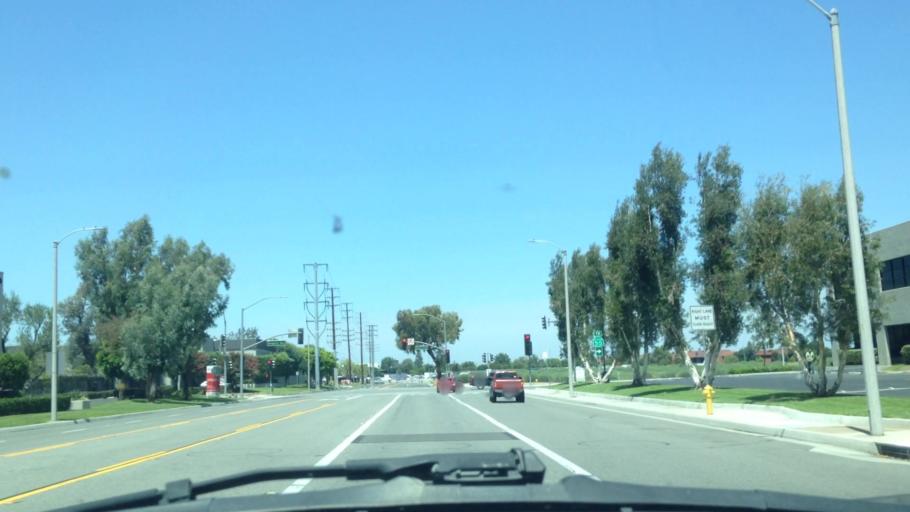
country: US
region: California
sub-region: Orange County
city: Tustin
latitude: 33.7193
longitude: -117.8355
